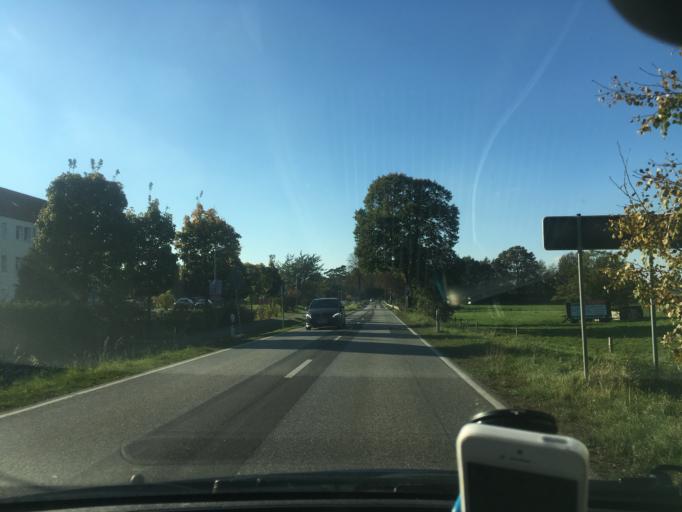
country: DE
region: Mecklenburg-Vorpommern
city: Wittenburg
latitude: 53.5191
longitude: 11.0121
